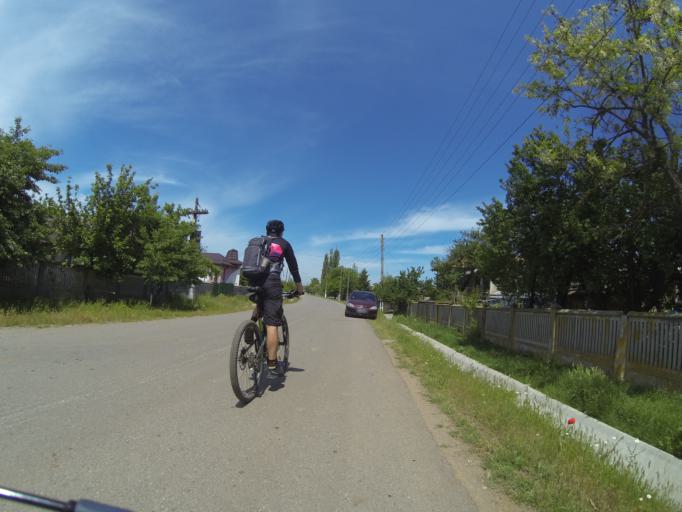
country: RO
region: Dolj
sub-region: Comuna Diosti
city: Radomir
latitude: 44.1569
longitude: 24.1633
